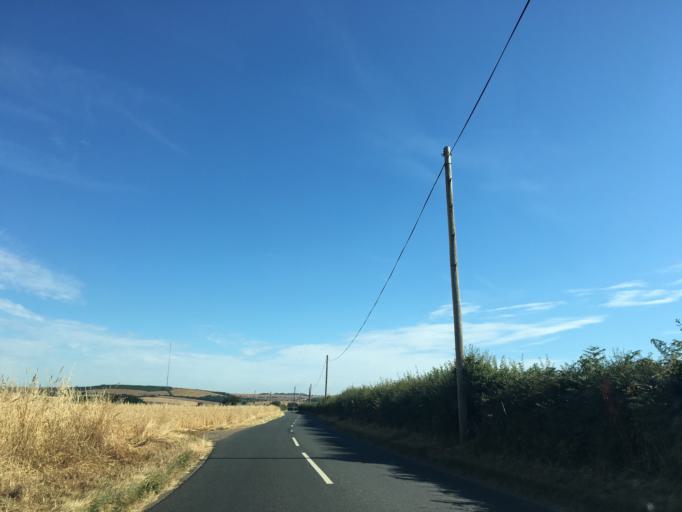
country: GB
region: England
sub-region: Isle of Wight
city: Chale
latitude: 50.6215
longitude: -1.3206
